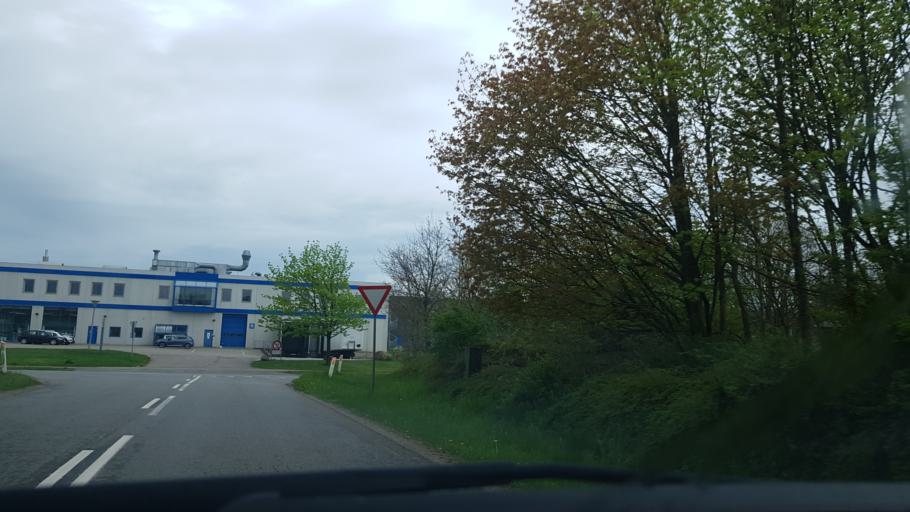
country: DK
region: South Denmark
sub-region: Kolding Kommune
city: Vamdrup
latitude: 55.4376
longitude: 9.2995
